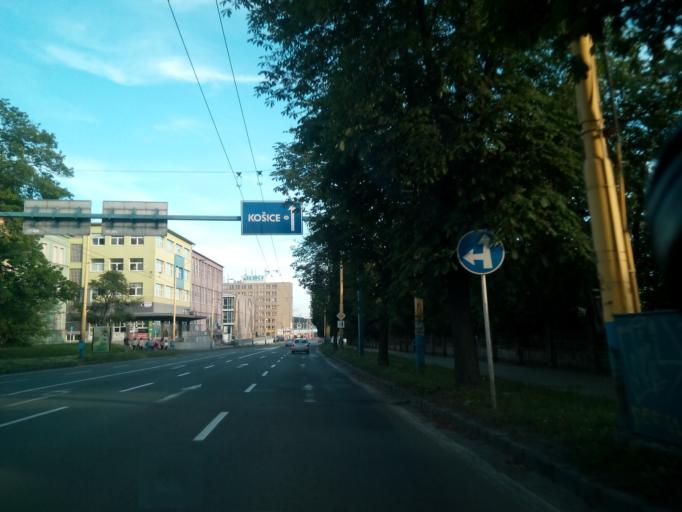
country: SK
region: Presovsky
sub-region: Okres Presov
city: Presov
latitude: 48.9875
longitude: 21.2483
